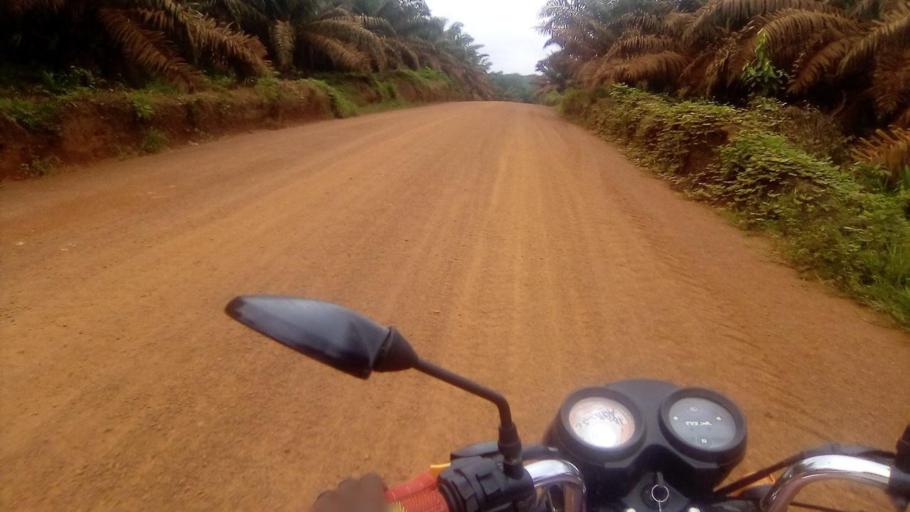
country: SL
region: Southern Province
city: Tongole
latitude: 7.4358
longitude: -11.8604
